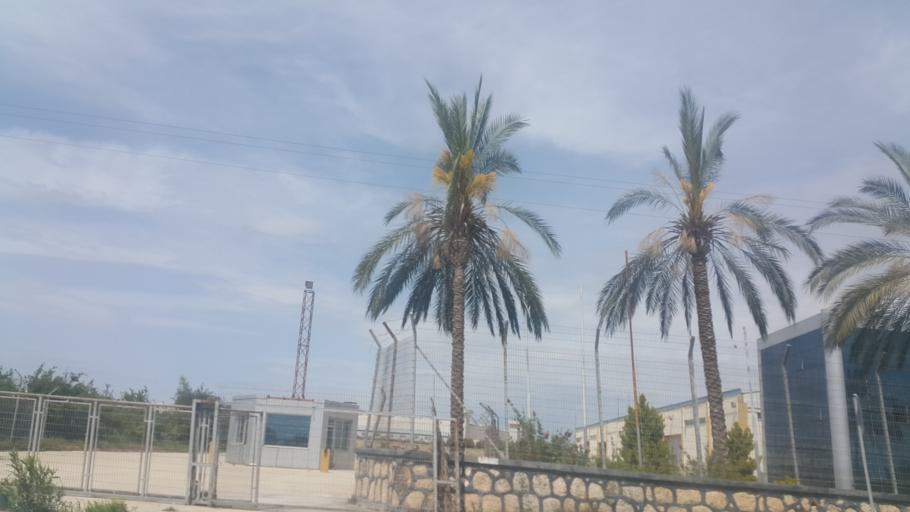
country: TR
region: Adana
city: Yakapinar
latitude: 36.9718
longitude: 35.5178
